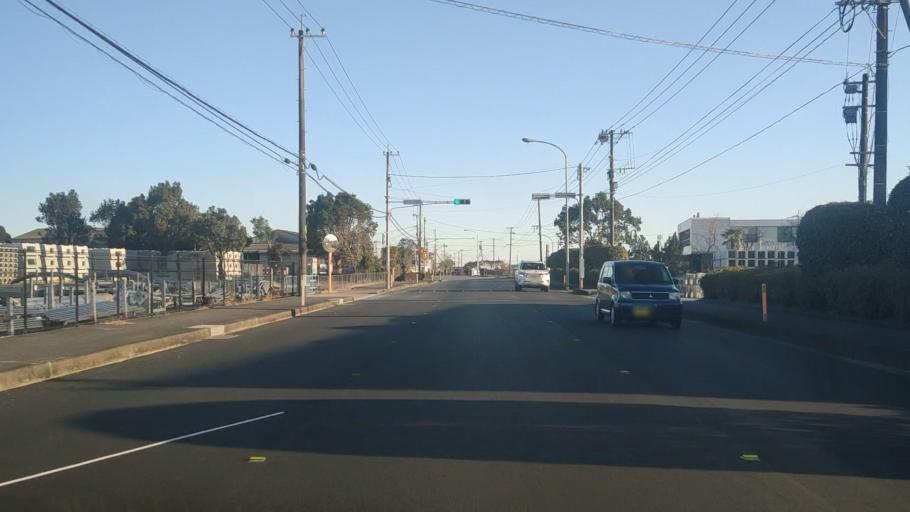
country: JP
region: Miyazaki
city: Takanabe
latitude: 32.2298
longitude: 131.5474
